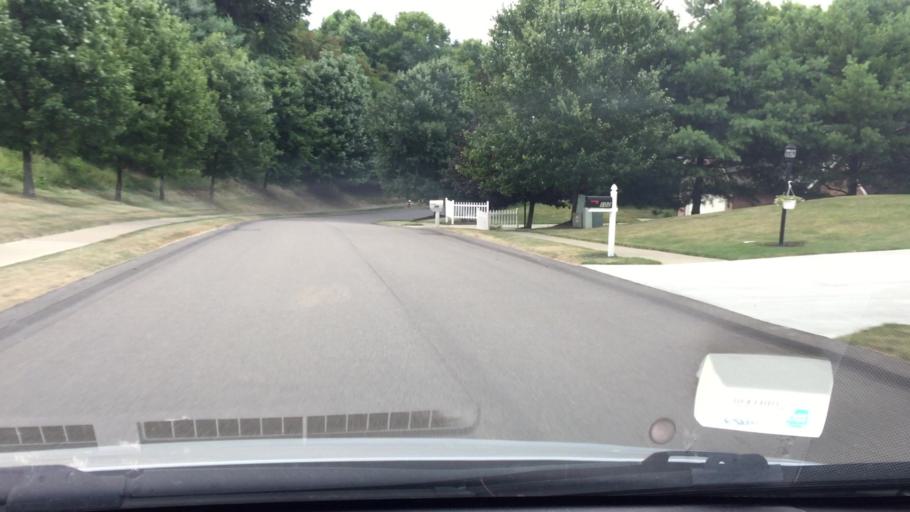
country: US
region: Pennsylvania
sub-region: Allegheny County
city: Bradford Woods
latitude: 40.6083
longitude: -80.0476
